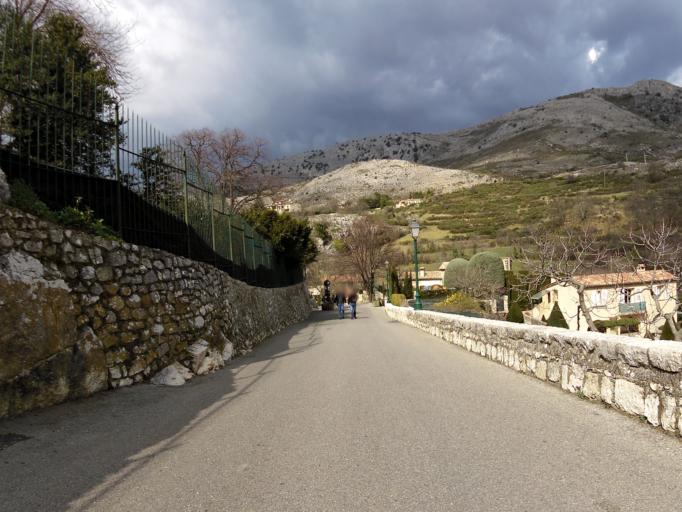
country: FR
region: Provence-Alpes-Cote d'Azur
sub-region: Departement des Alpes-Maritimes
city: Opio
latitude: 43.7206
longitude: 6.9782
